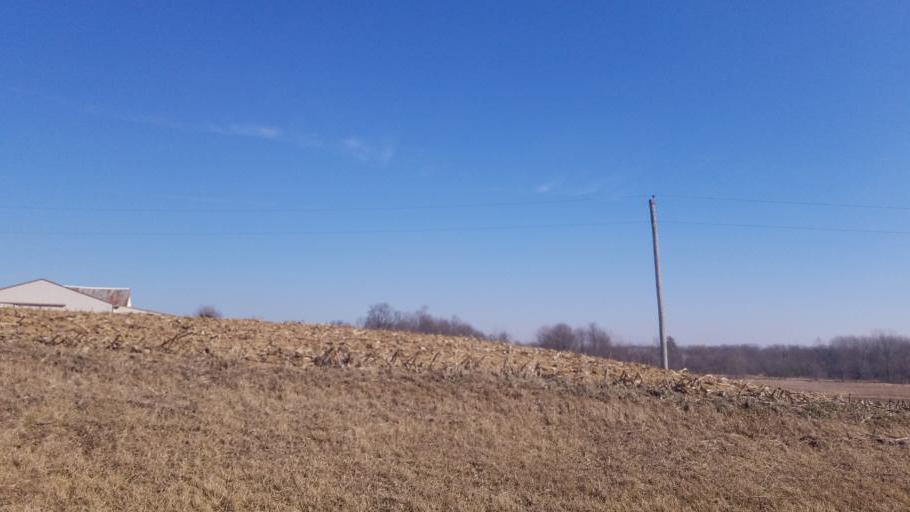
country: US
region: Ohio
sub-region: Richland County
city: Shelby
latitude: 40.9126
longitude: -82.5675
